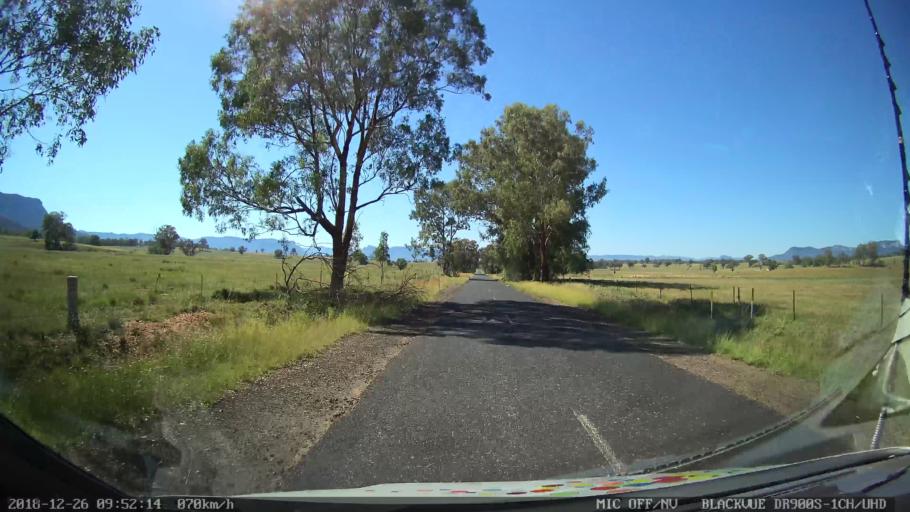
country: AU
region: New South Wales
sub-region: Mid-Western Regional
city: Kandos
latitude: -33.0086
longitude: 150.1481
